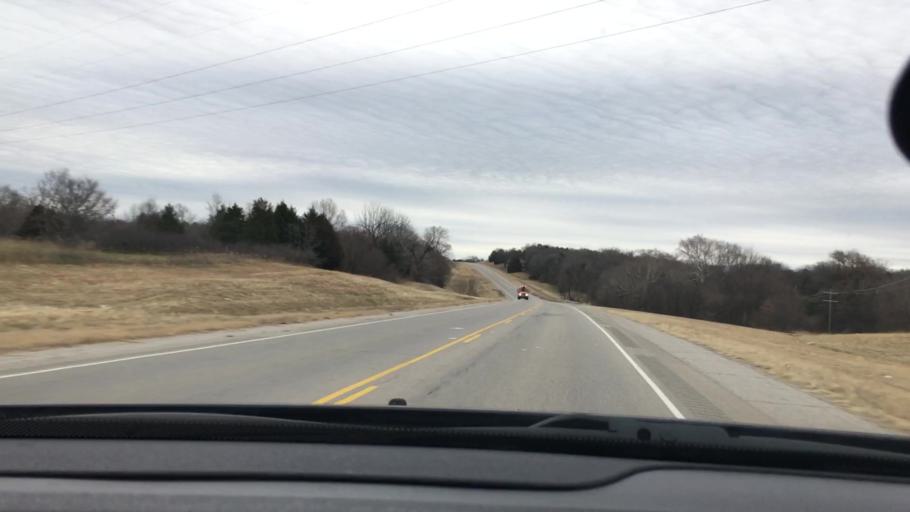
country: US
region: Oklahoma
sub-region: Johnston County
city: Tishomingo
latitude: 34.2342
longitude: -96.7842
